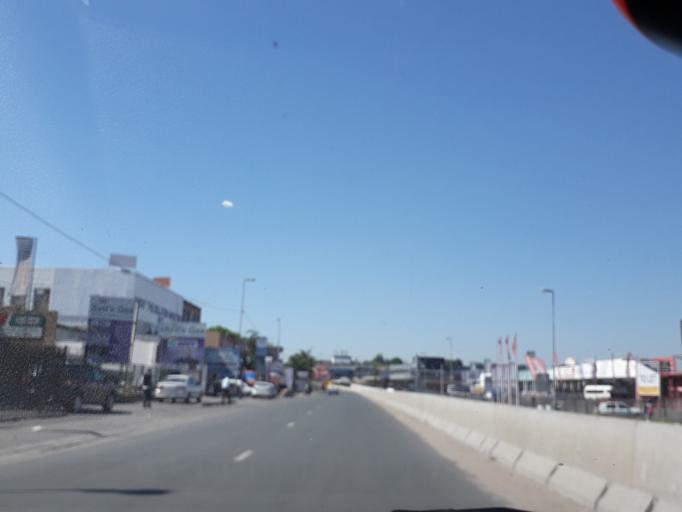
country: ZA
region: Gauteng
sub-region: City of Johannesburg Metropolitan Municipality
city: Modderfontein
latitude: -26.1164
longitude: 28.0844
